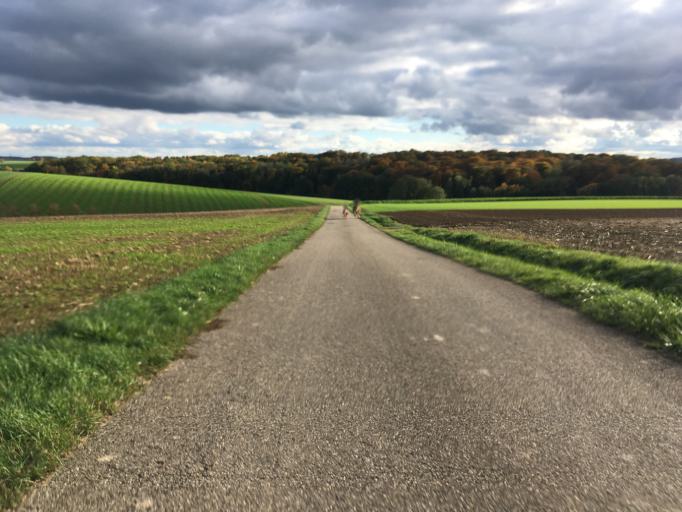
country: DE
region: Baden-Wuerttemberg
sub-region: Regierungsbezirk Stuttgart
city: Kuenzelsau
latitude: 49.2562
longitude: 9.6630
